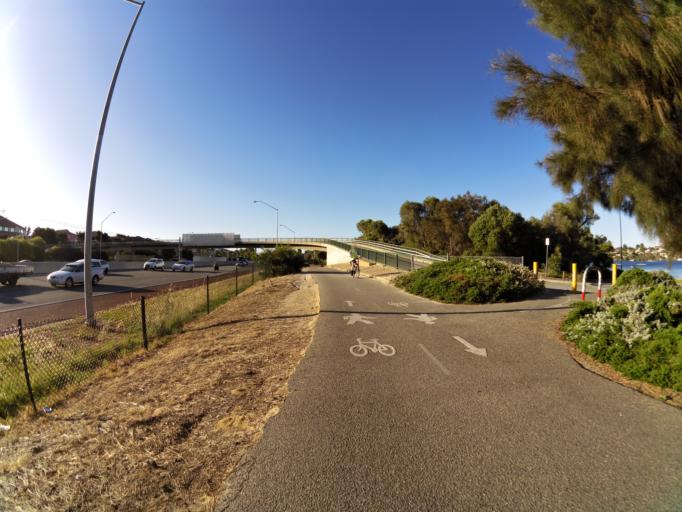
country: AU
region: Western Australia
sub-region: South Perth
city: Manning
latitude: -32.0169
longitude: 115.8573
